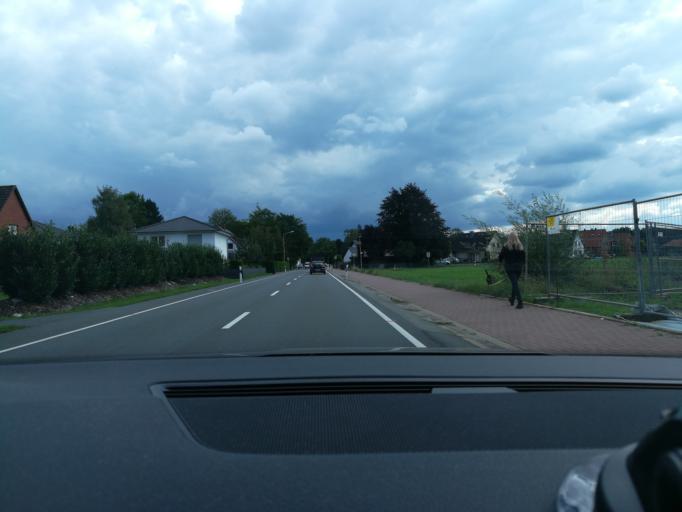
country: DE
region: North Rhine-Westphalia
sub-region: Regierungsbezirk Detmold
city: Minden
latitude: 52.3188
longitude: 8.8770
